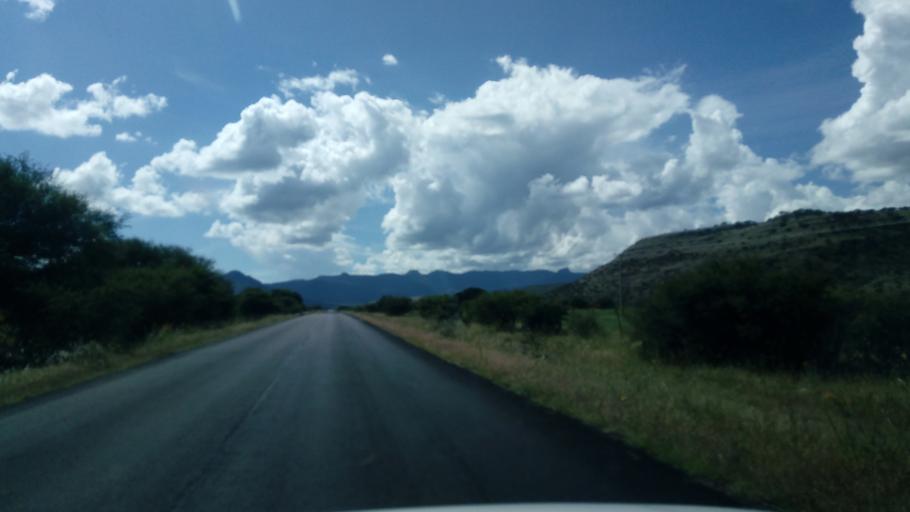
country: MX
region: Durango
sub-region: Durango
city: Jose Refugio Salcido
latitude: 23.8198
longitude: -104.4830
